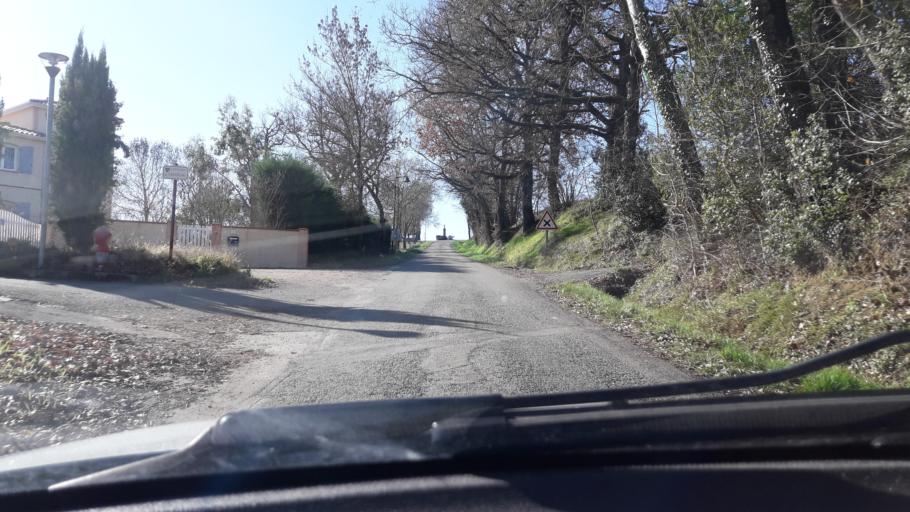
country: FR
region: Midi-Pyrenees
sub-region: Departement du Gers
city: Gimont
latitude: 43.6411
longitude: 1.0027
